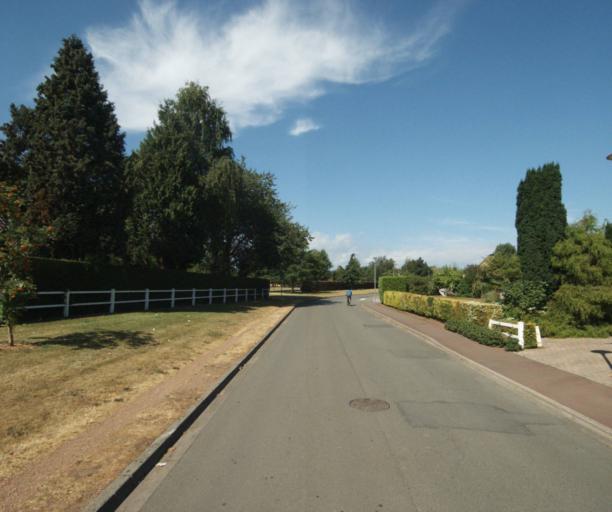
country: FR
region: Nord-Pas-de-Calais
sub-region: Departement du Nord
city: Halluin
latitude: 50.7707
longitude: 3.1210
